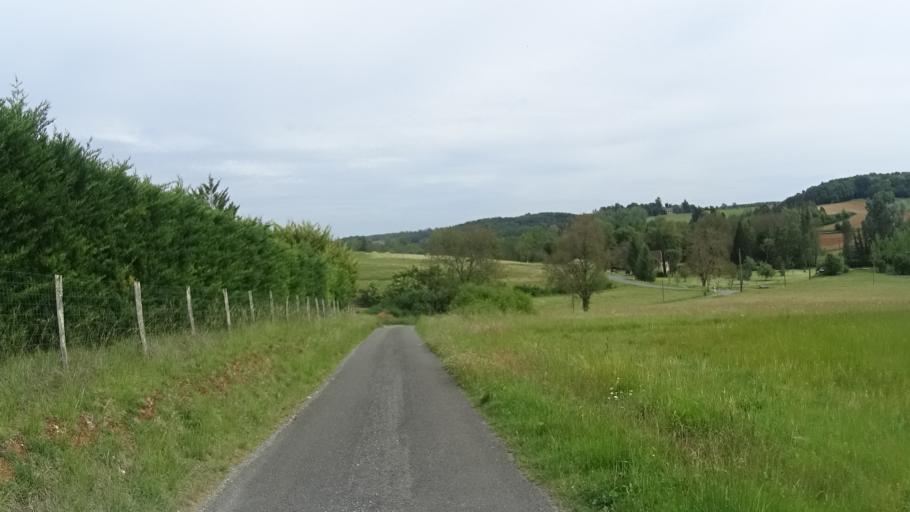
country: FR
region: Aquitaine
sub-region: Departement de la Dordogne
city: Lembras
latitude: 44.9950
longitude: 0.5350
